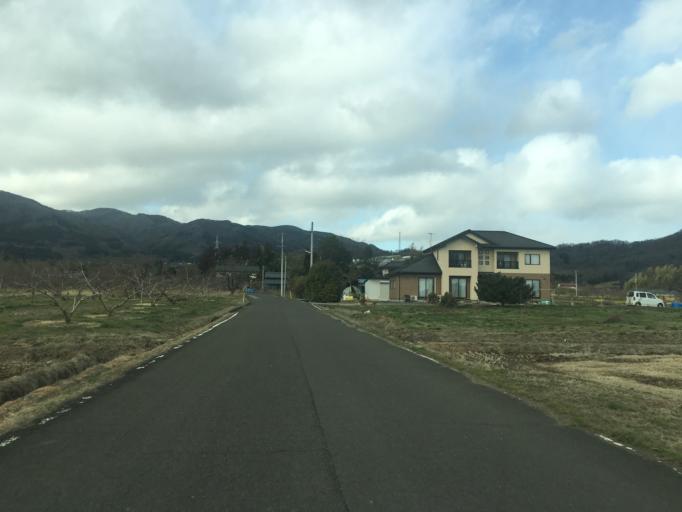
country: JP
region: Fukushima
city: Yanagawamachi-saiwaicho
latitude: 37.8859
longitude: 140.5819
